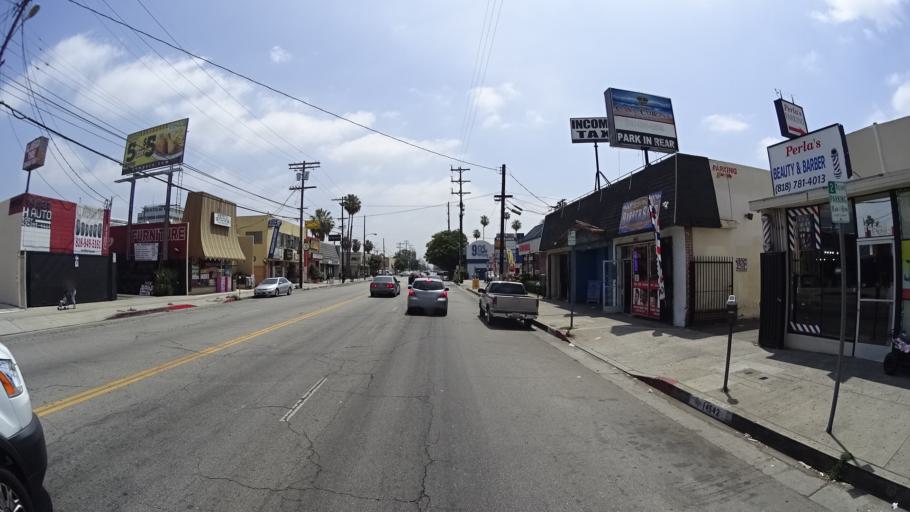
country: US
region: California
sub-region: Los Angeles County
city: Van Nuys
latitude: 34.1939
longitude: -118.4503
